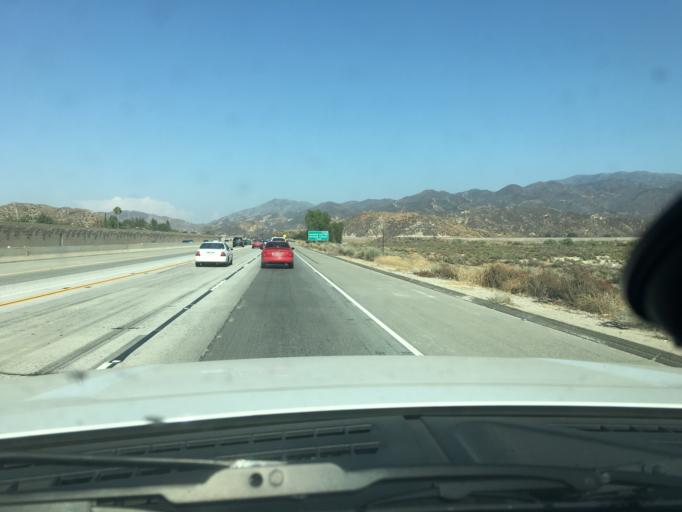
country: US
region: California
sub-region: Los Angeles County
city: Agua Dulce
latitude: 34.4276
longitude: -118.4143
